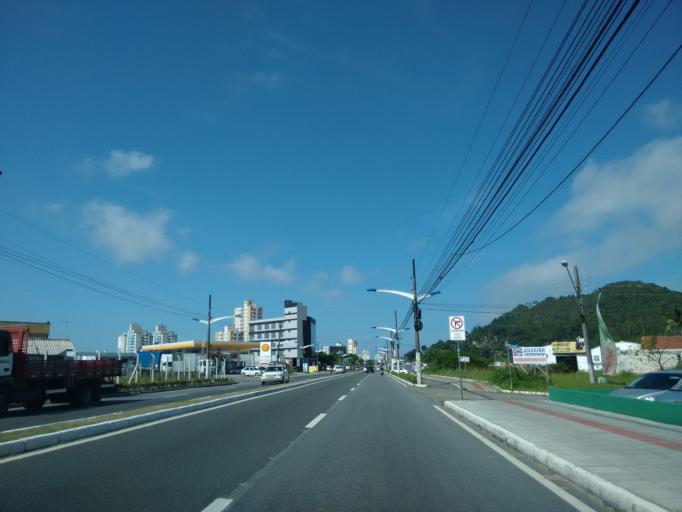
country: BR
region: Santa Catarina
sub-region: Itajai
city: Itajai
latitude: -26.9233
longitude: -48.6757
